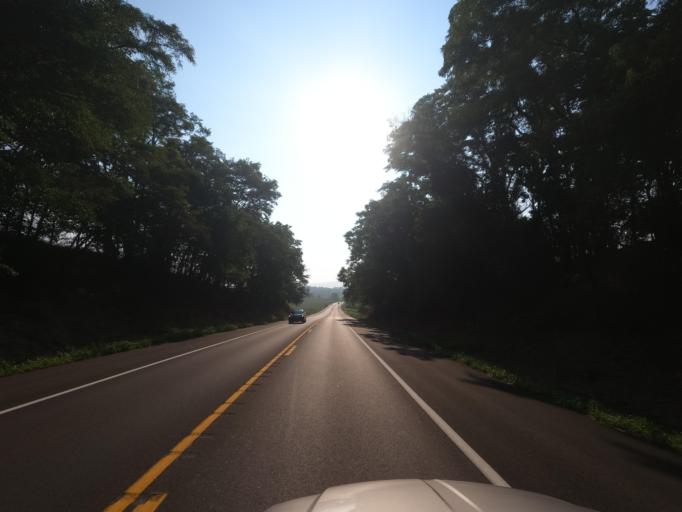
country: US
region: Pennsylvania
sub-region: Franklin County
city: Wayne Heights
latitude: 39.7077
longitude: -77.5841
